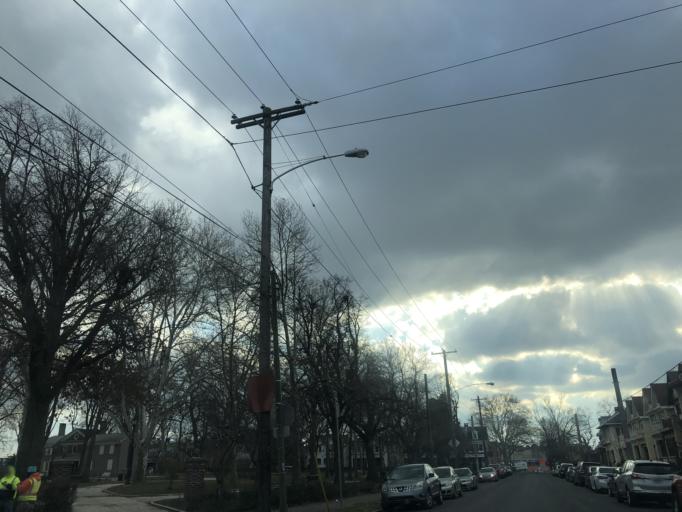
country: US
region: Pennsylvania
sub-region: Philadelphia County
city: Philadelphia
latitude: 39.9212
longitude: -75.1838
